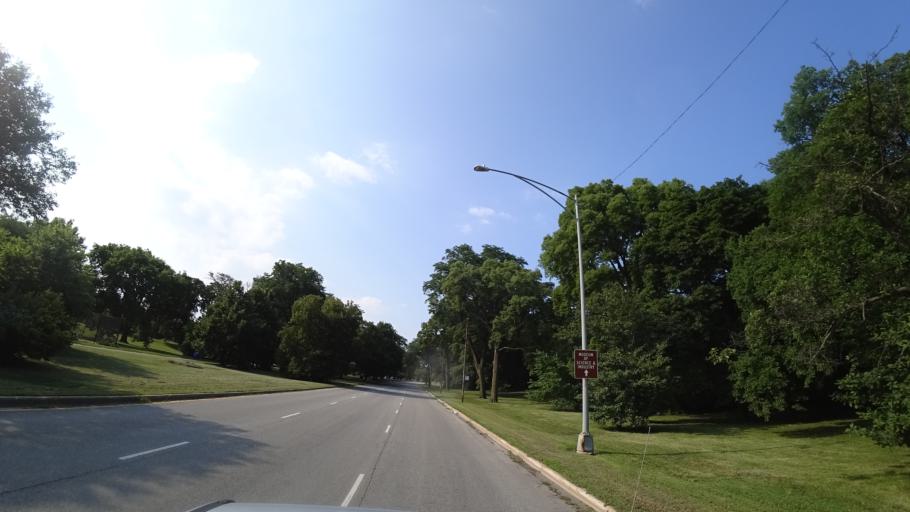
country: US
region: Illinois
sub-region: Cook County
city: Chicago
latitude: 41.7754
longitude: -87.5848
